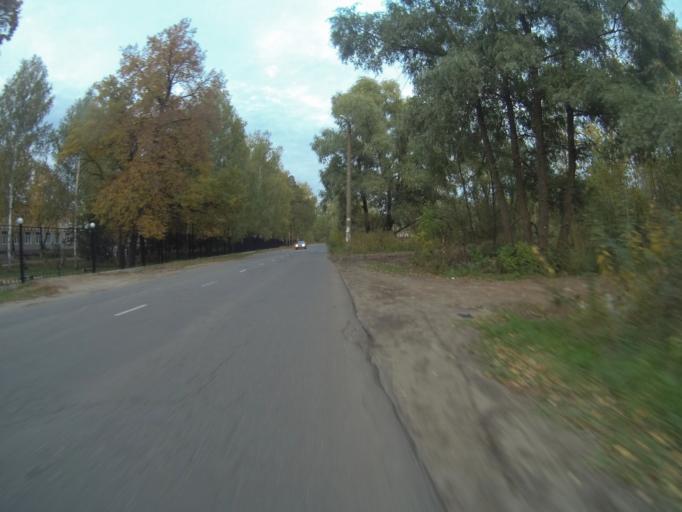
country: RU
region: Vladimir
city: Sobinka
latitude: 56.0012
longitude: 40.0572
